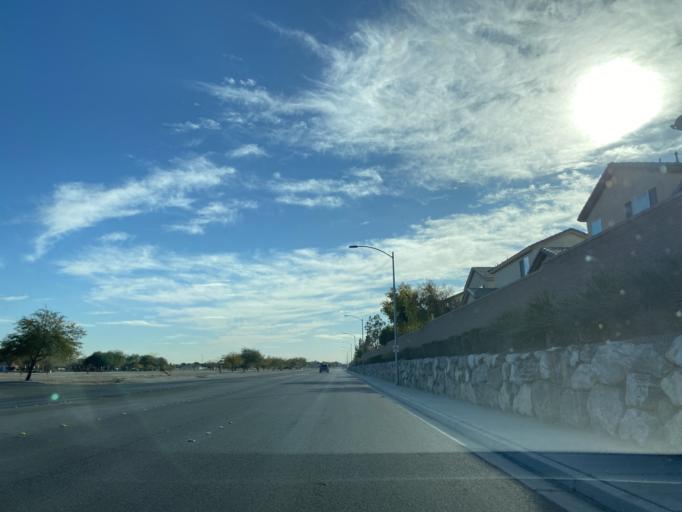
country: US
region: Nevada
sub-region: Clark County
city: North Las Vegas
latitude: 36.3090
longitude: -115.2423
